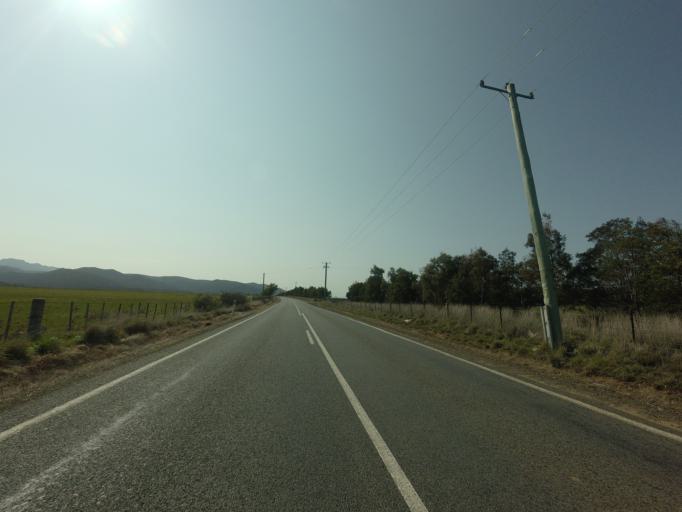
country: AU
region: Tasmania
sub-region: Northern Midlands
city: Evandale
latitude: -41.7955
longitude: 147.7077
